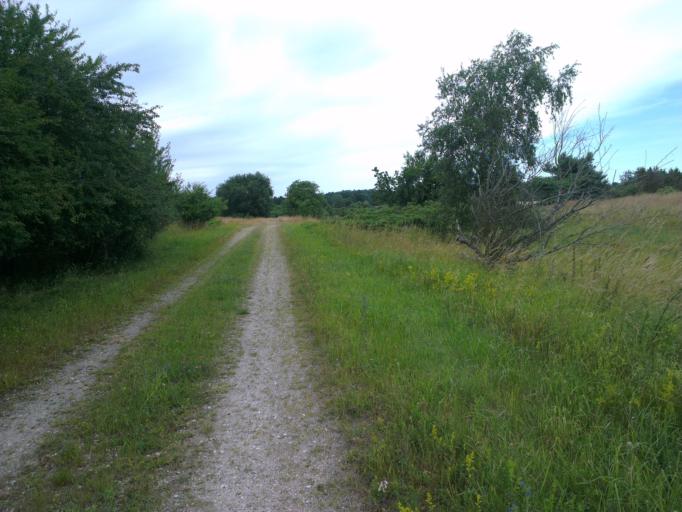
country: DK
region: Capital Region
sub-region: Frederikssund Kommune
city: Jaegerspris
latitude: 55.8983
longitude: 11.9294
